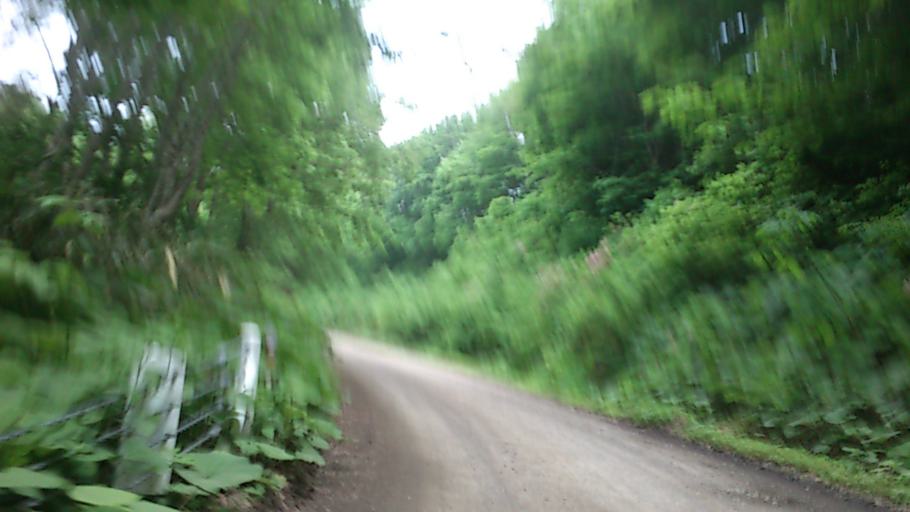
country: JP
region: Aomori
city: Hirosaki
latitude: 40.5609
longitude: 140.1805
